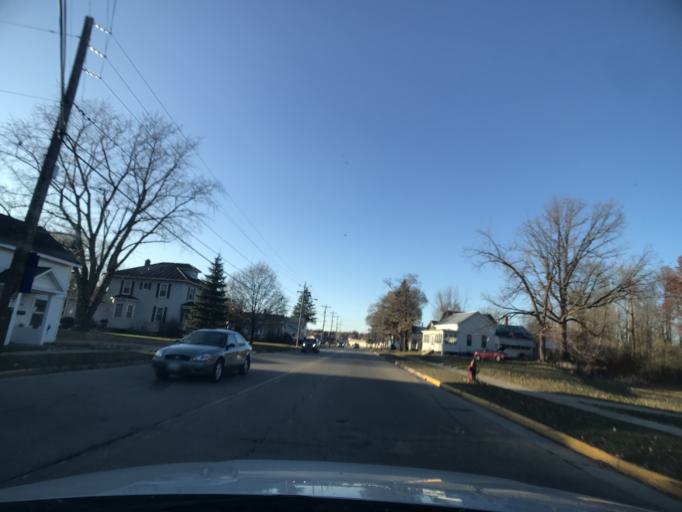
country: US
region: Wisconsin
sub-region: Oconto County
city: Oconto
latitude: 44.8918
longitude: -87.8801
